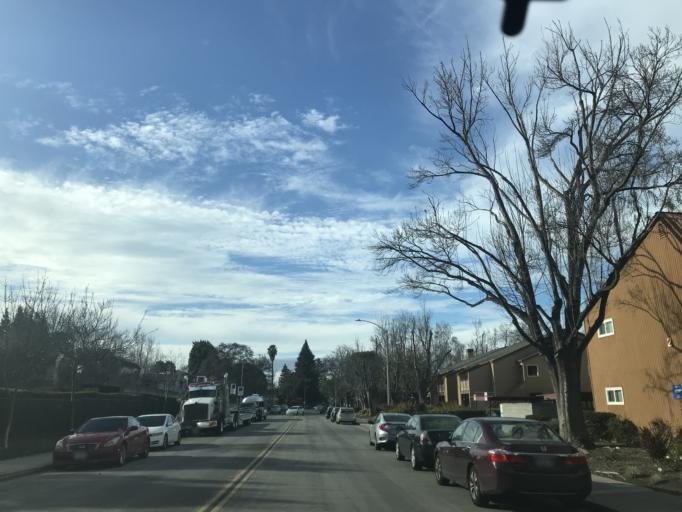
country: US
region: California
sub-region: Santa Clara County
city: Sunnyvale
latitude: 37.3884
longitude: -122.0437
